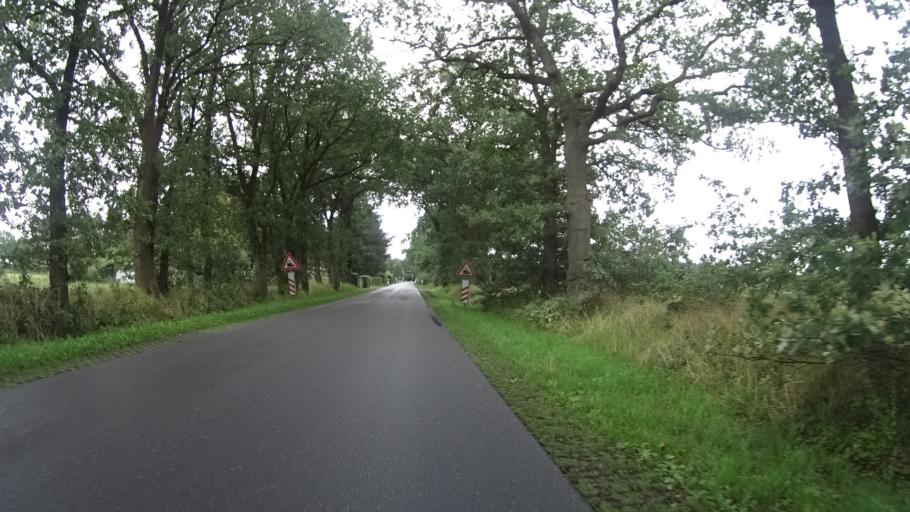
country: DE
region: Schleswig-Holstein
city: Henstedt-Ulzburg
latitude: 53.7735
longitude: 9.9704
